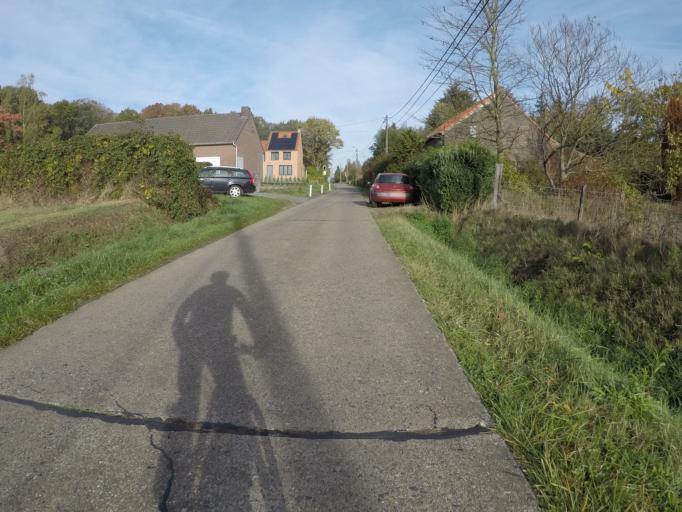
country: BE
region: Flanders
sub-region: Provincie Vlaams-Brabant
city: Begijnendijk
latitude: 51.0017
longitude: 4.7705
